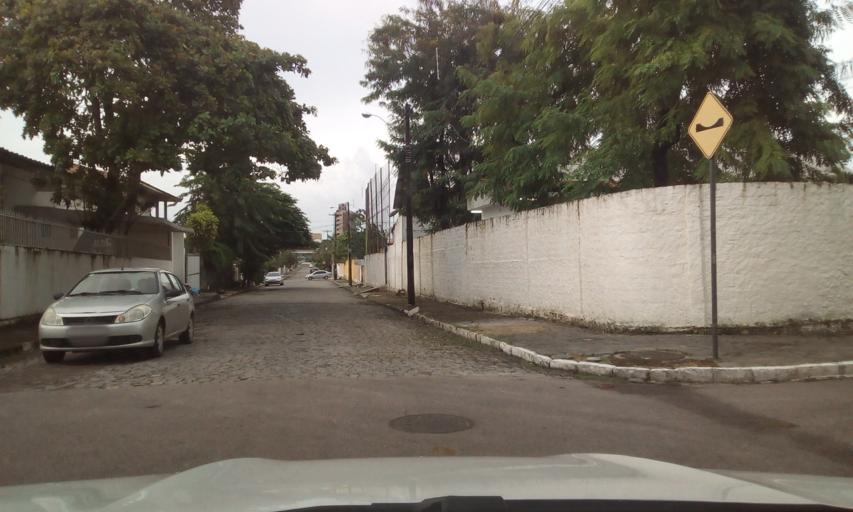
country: BR
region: Paraiba
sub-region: Joao Pessoa
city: Joao Pessoa
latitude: -7.1147
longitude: -34.8572
